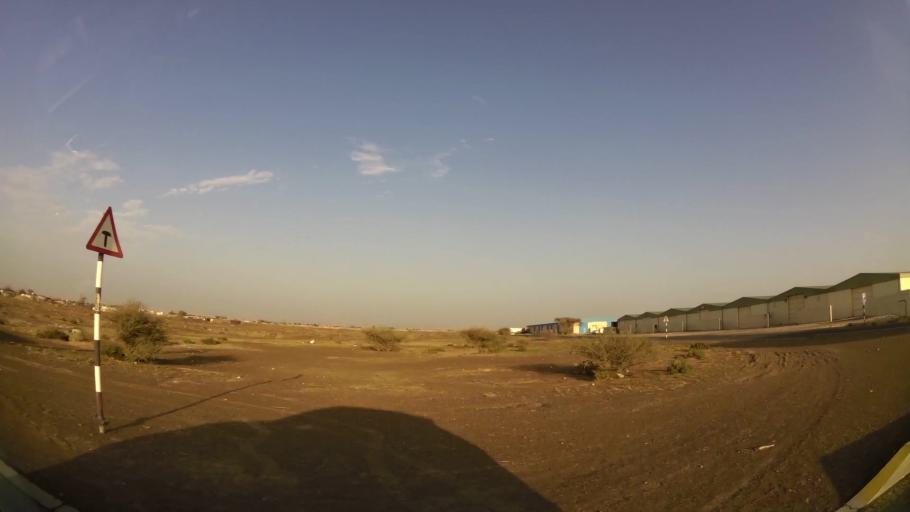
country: AE
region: Abu Dhabi
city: Al Ain
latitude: 24.1551
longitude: 55.8330
